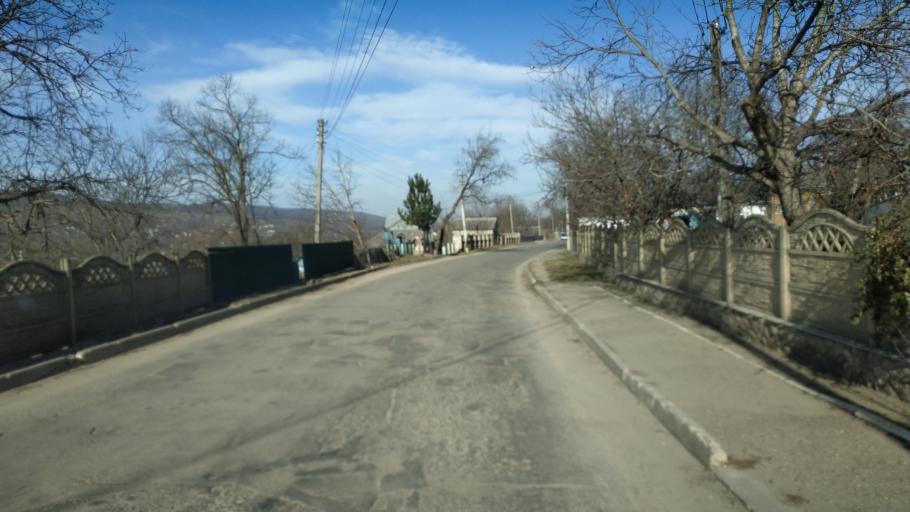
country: MD
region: Chisinau
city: Vatra
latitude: 47.0224
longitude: 28.6425
